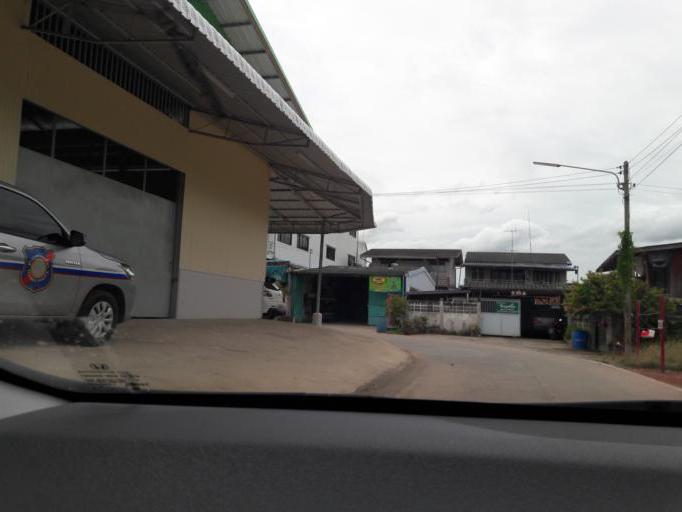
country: TH
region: Samut Sakhon
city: Ban Phaeo
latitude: 13.5547
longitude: 100.0384
